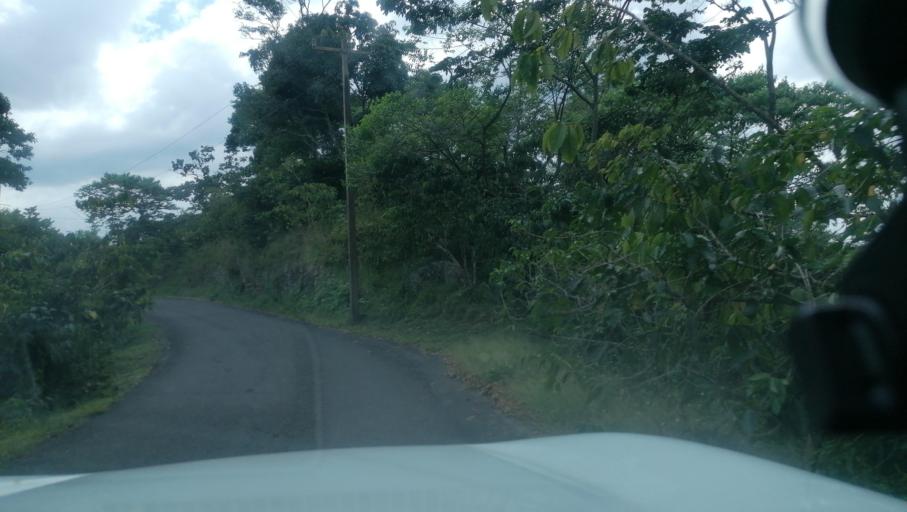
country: MX
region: Chiapas
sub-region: Cacahoatan
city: Benito Juarez
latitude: 15.0575
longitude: -92.1512
